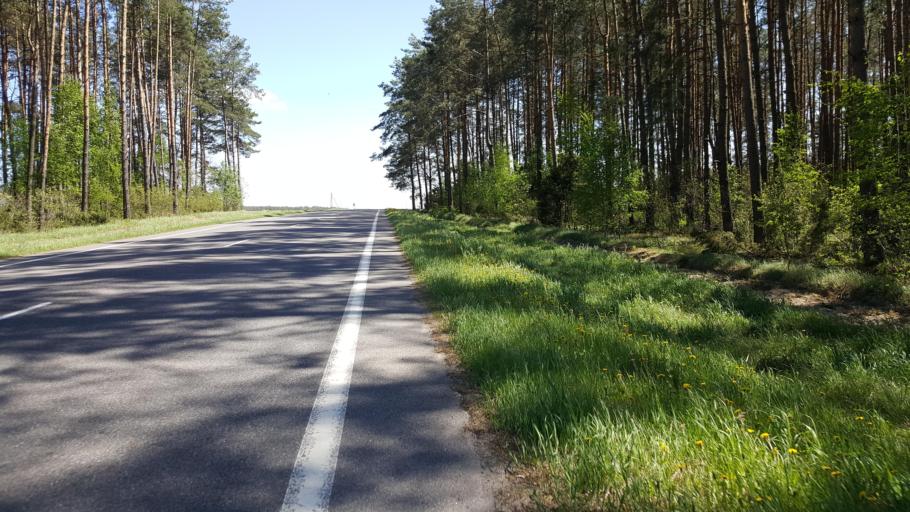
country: BY
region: Brest
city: Kamyanyets
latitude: 52.4757
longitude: 23.8122
